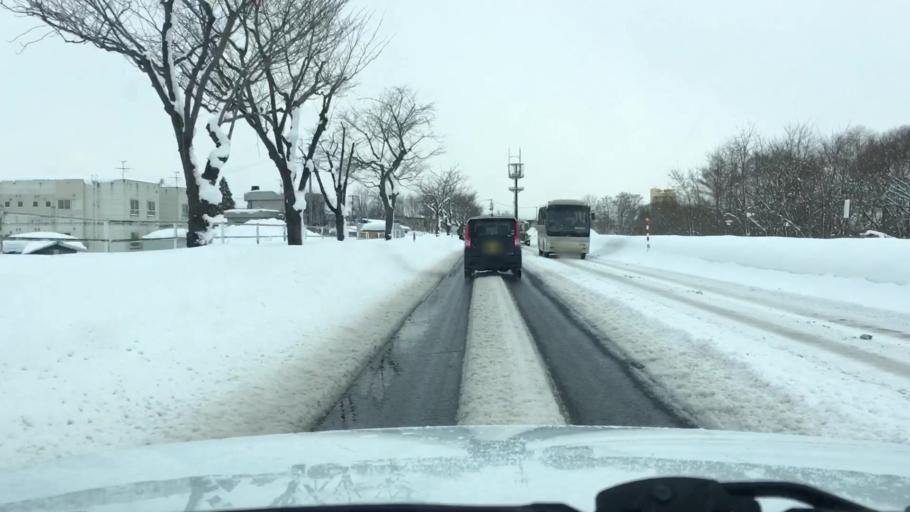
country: JP
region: Aomori
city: Hirosaki
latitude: 40.6127
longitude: 140.4555
